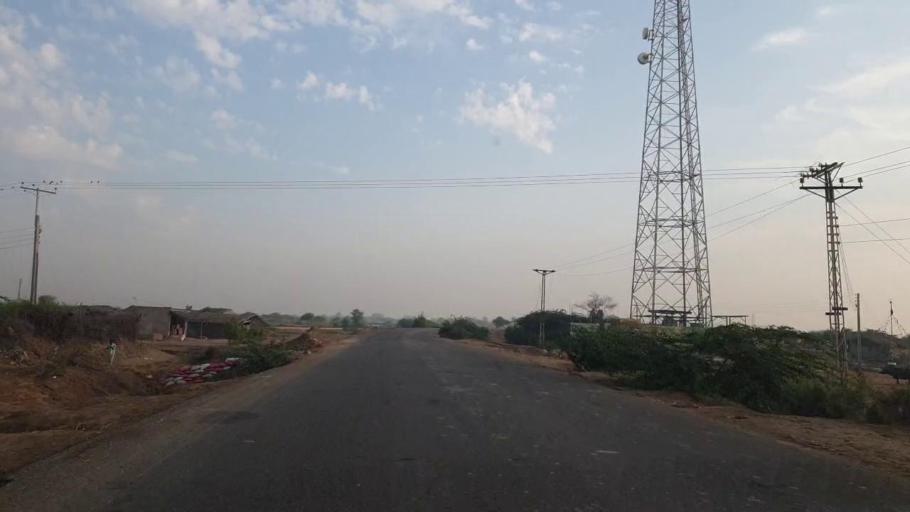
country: PK
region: Sindh
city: Badin
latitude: 24.6987
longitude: 68.9217
